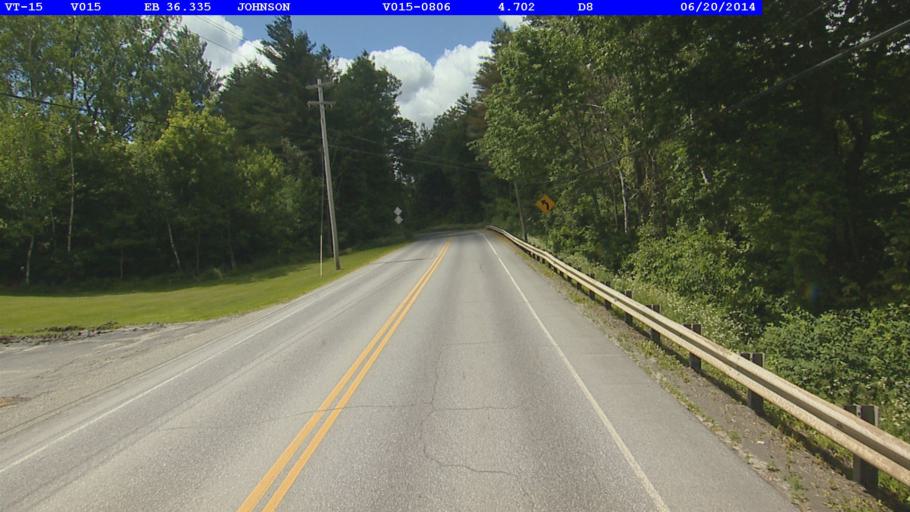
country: US
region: Vermont
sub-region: Lamoille County
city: Johnson
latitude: 44.6280
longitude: -72.6769
